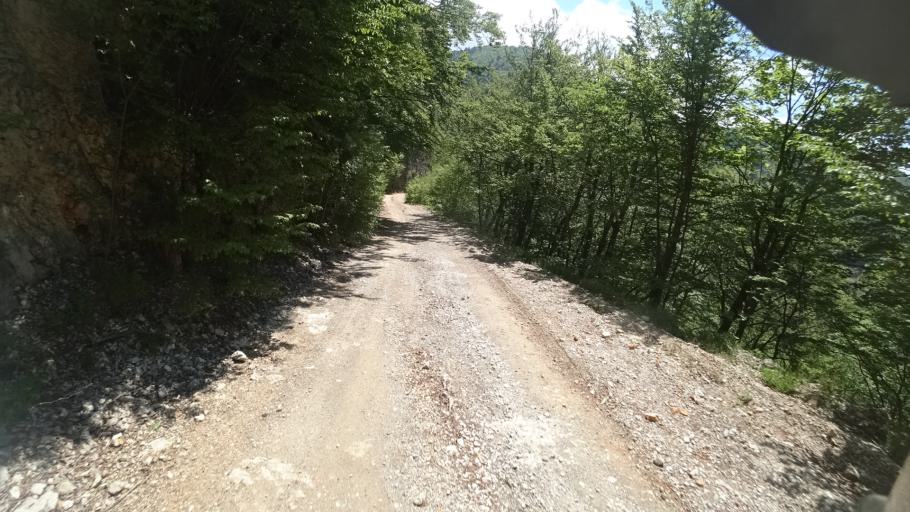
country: BA
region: Federation of Bosnia and Herzegovina
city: Orasac
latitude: 44.5774
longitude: 15.8571
